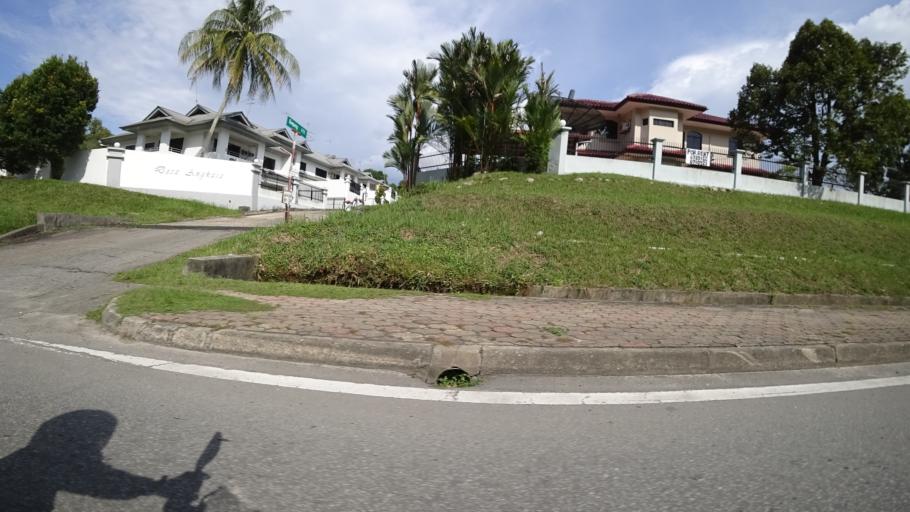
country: BN
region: Brunei and Muara
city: Bandar Seri Begawan
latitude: 4.8571
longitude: 114.8929
